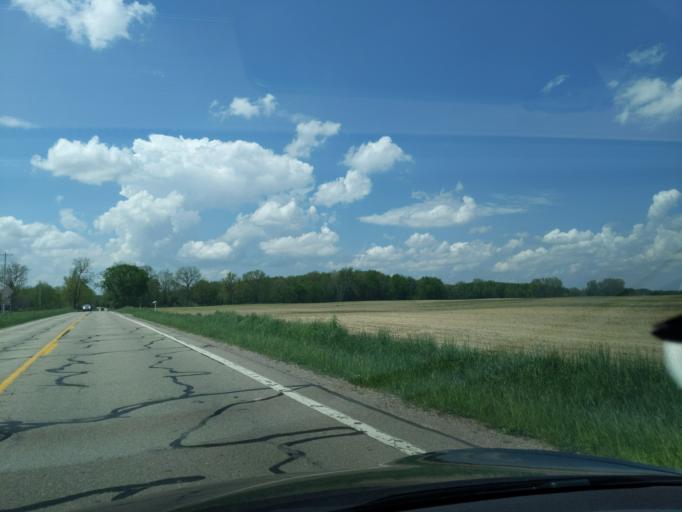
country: US
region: Michigan
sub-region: Ingham County
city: Stockbridge
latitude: 42.4972
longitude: -84.1224
